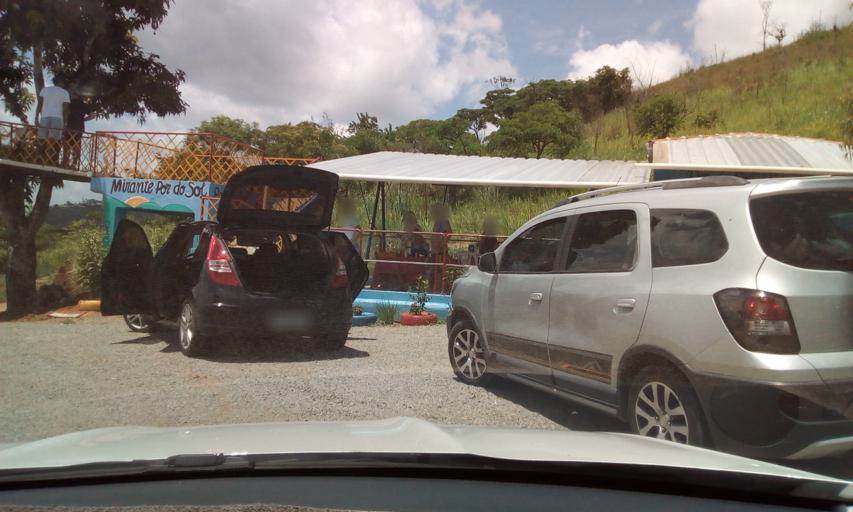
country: BR
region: Pernambuco
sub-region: Bonito
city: Bonito
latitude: -8.4893
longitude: -35.7232
